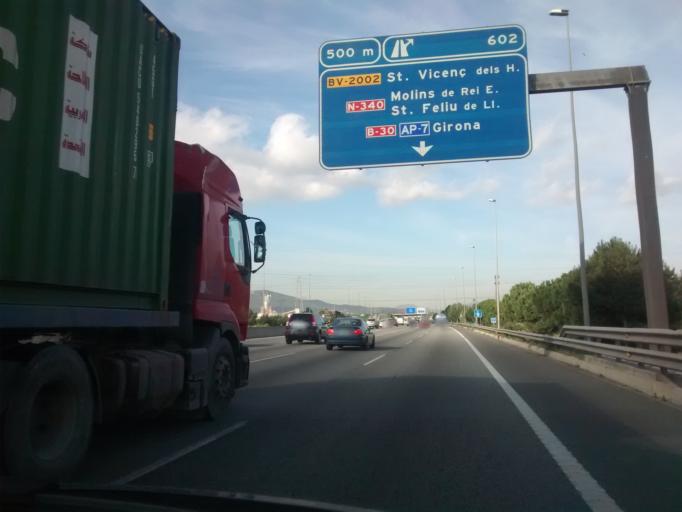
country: ES
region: Catalonia
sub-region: Provincia de Barcelona
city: Santa Coloma de Cervello
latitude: 41.3828
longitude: 2.0234
